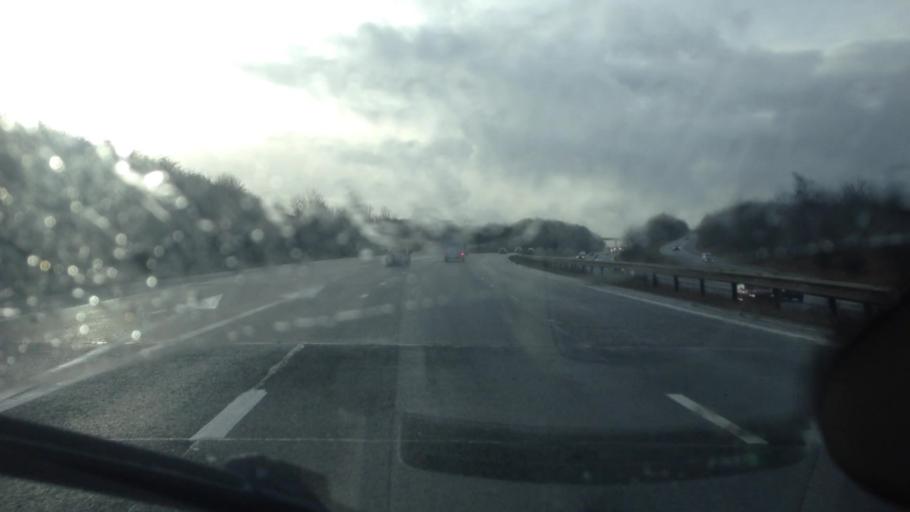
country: GB
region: England
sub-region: City and Borough of Wakefield
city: Crigglestone
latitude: 53.6289
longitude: -1.5408
